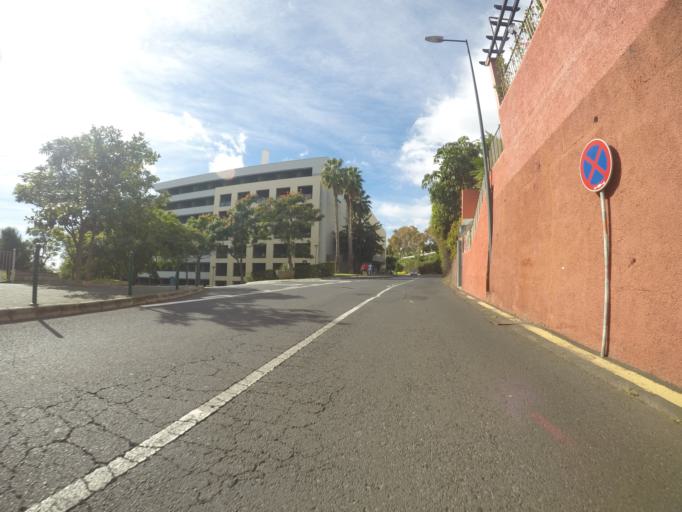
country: PT
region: Madeira
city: Camara de Lobos
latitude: 32.6381
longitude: -16.9347
